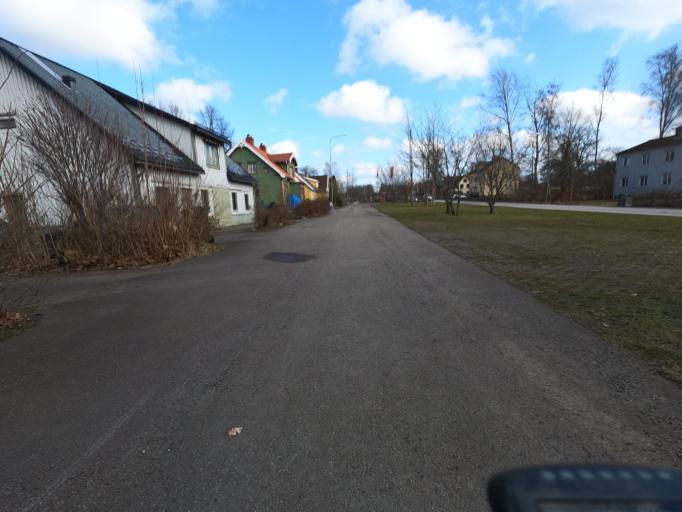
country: SE
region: Kronoberg
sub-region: Alvesta Kommun
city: Vislanda
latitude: 56.7378
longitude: 14.5407
